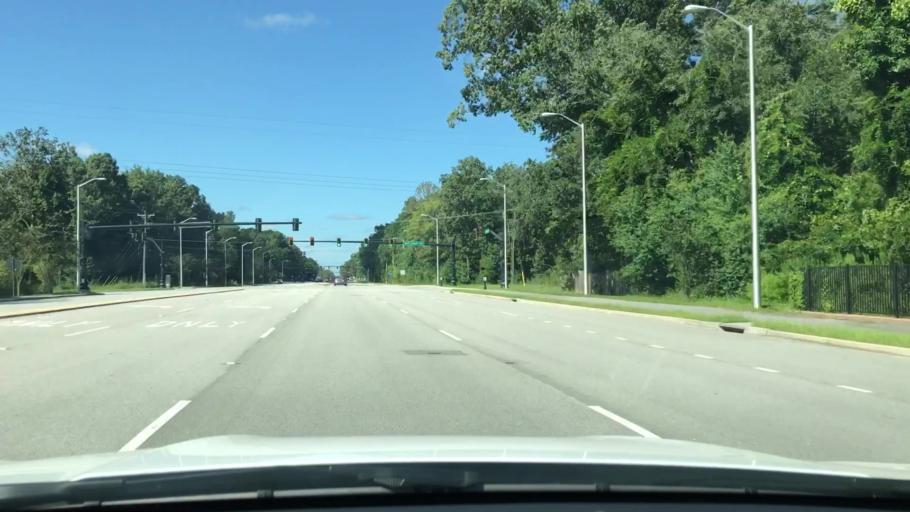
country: US
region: South Carolina
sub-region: Charleston County
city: Shell Point
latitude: 32.8285
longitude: -80.0762
